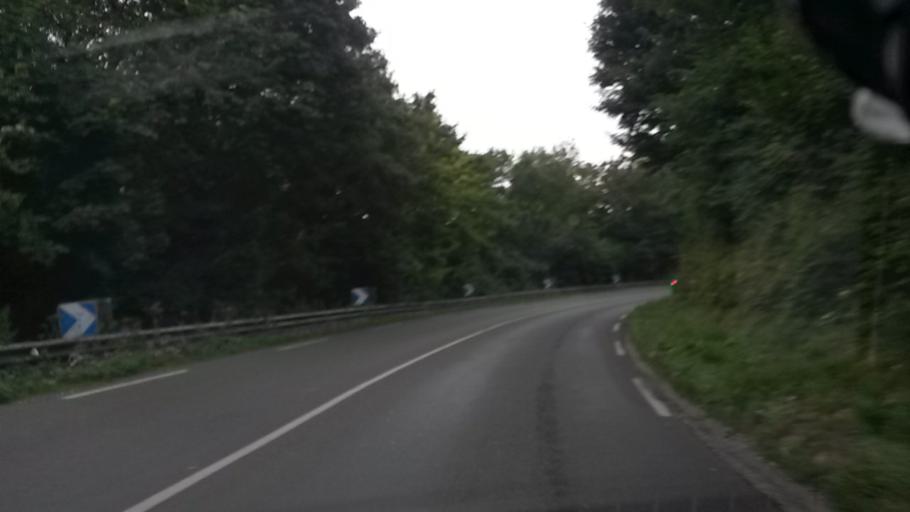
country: FR
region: Haute-Normandie
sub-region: Departement de la Seine-Maritime
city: Aumale
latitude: 49.7648
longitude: 1.7803
